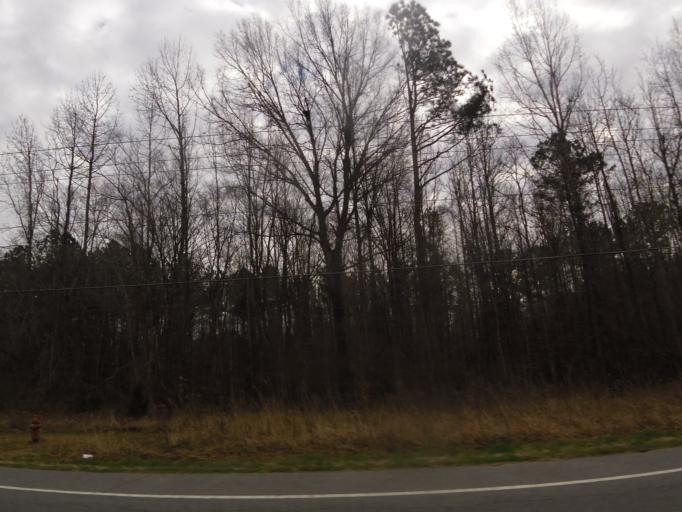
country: US
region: North Carolina
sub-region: Hertford County
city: Murfreesboro
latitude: 36.3241
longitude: -77.2254
